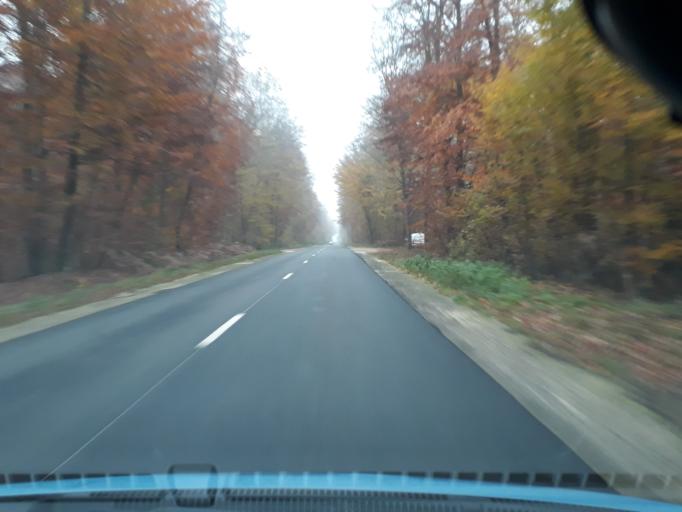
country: FR
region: Ile-de-France
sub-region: Departement de Seine-et-Marne
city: Thomery
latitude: 48.3915
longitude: 2.7724
